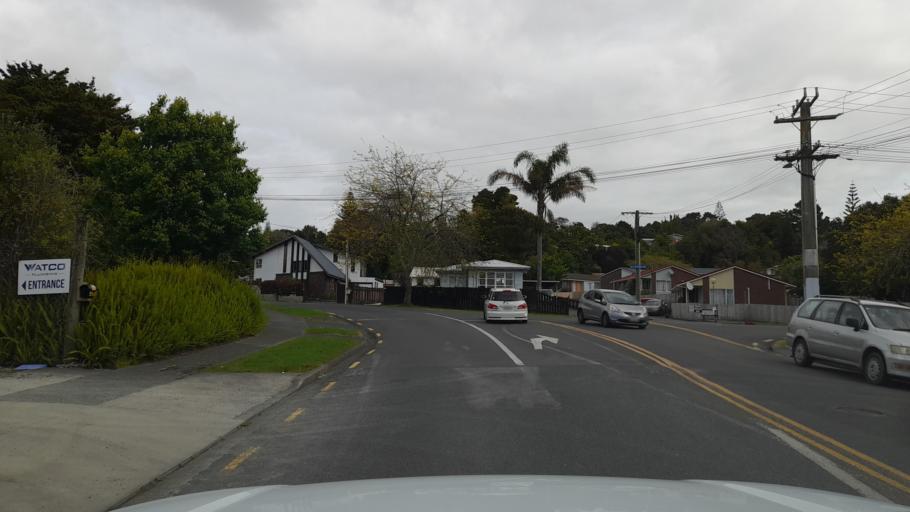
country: NZ
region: Northland
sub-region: Whangarei
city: Whangarei
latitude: -35.7344
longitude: 174.3209
